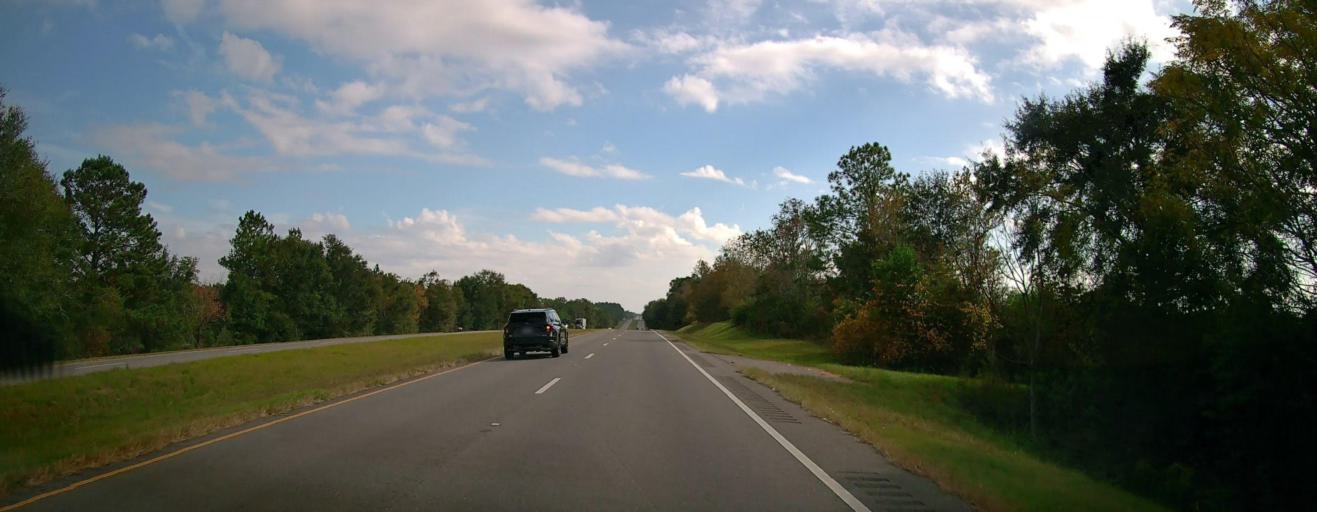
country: US
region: Georgia
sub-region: Thomas County
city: Meigs
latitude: 30.9906
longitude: -84.0435
